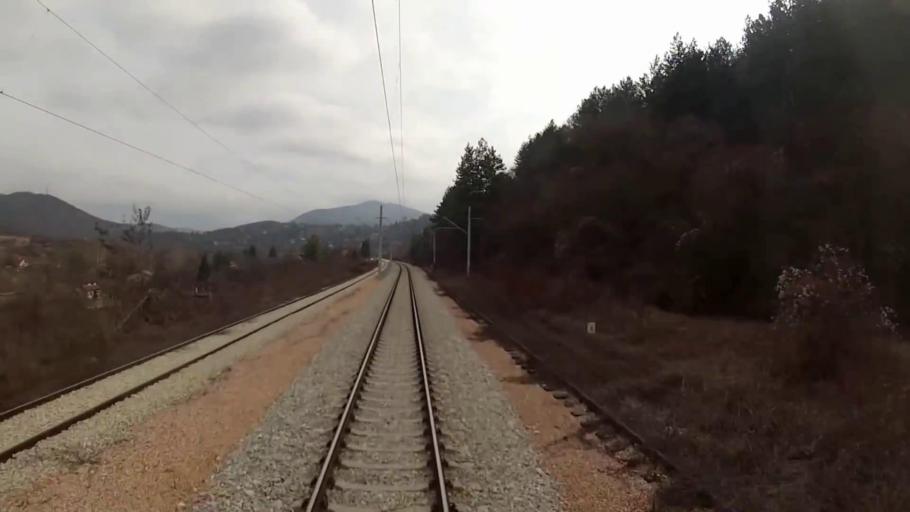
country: BG
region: Sofiya
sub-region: Obshtina Gorna Malina
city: Gorna Malina
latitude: 42.6912
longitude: 23.8135
